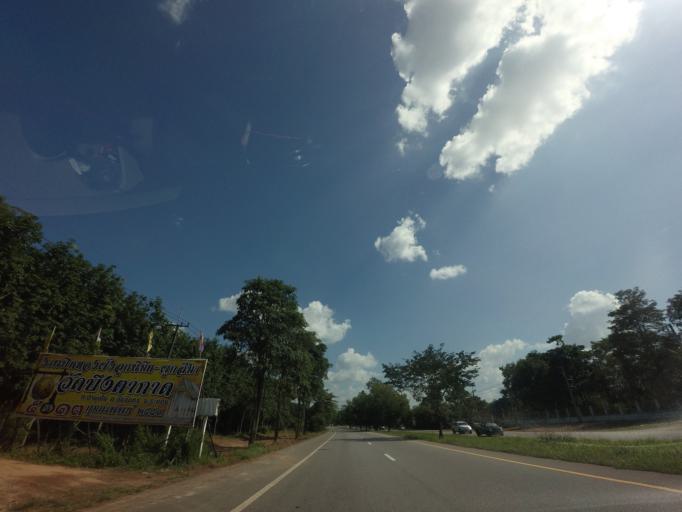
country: TH
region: Rayong
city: Wang Chan
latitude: 12.9695
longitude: 101.4962
